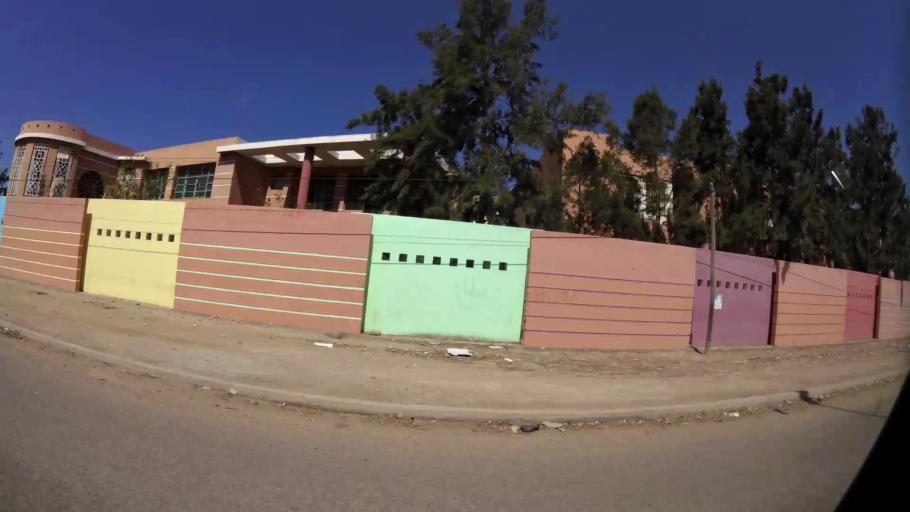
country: MA
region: Souss-Massa-Draa
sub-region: Inezgane-Ait Mellou
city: Inezgane
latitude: 30.3281
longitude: -9.5068
